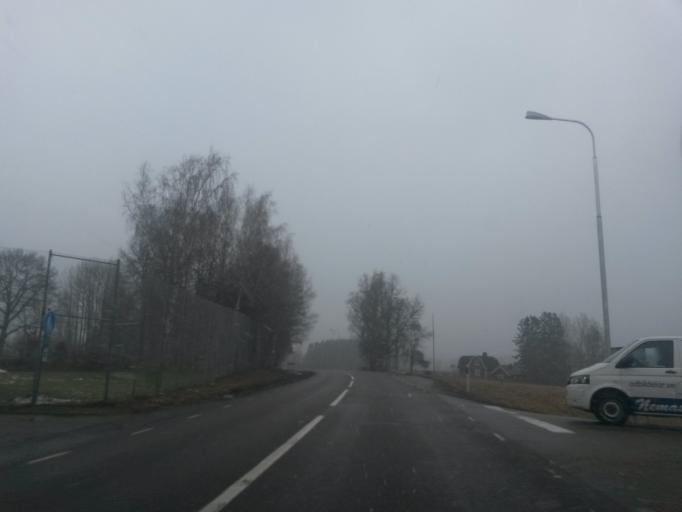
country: SE
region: Vaestra Goetaland
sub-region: Vanersborgs Kommun
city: Vargon
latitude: 58.2426
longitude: 12.4240
